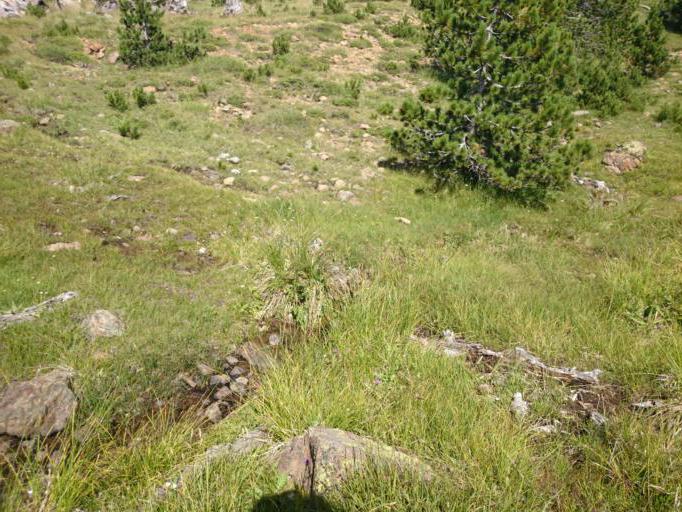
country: AL
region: Elbasan
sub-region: Rrethi i Gramshit
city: Lenias
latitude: 40.8197
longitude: 20.4540
